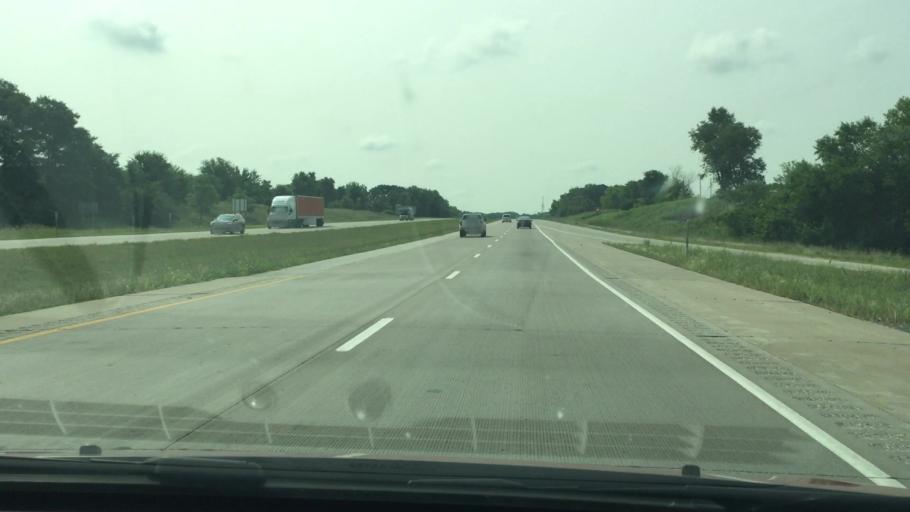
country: US
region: Iowa
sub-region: Scott County
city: Buffalo
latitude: 41.5357
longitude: -90.6762
